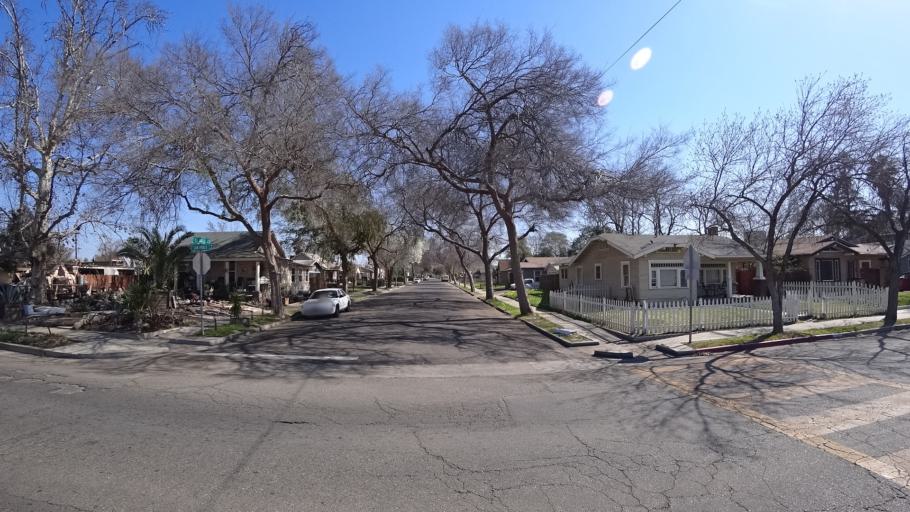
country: US
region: California
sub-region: Fresno County
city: Fresno
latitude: 36.7550
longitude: -119.7951
